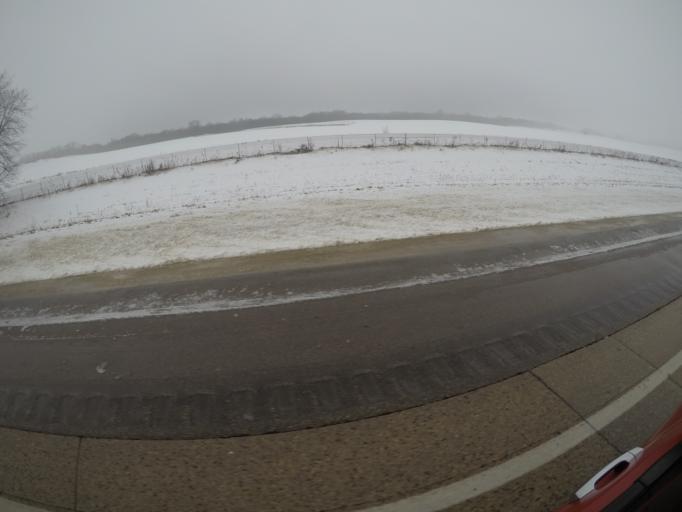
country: US
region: Minnesota
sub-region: Goodhue County
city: Pine Island
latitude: 44.1918
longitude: -92.5948
